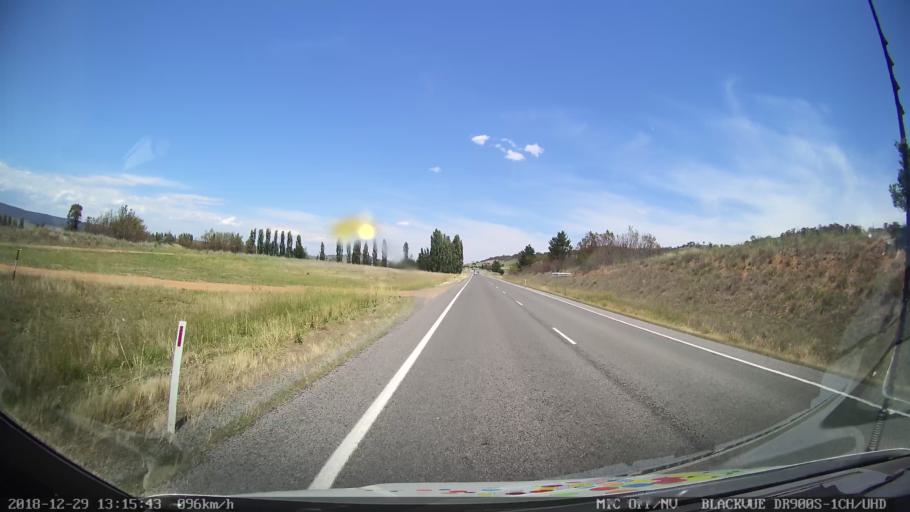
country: AU
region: Australian Capital Territory
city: Macarthur
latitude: -35.7130
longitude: 149.1587
